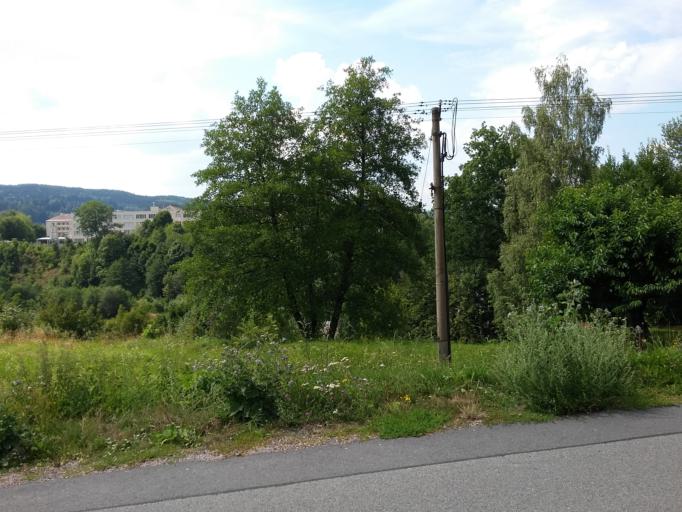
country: CZ
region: Pardubicky
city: Ceska Trebova
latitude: 49.9058
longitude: 16.4512
